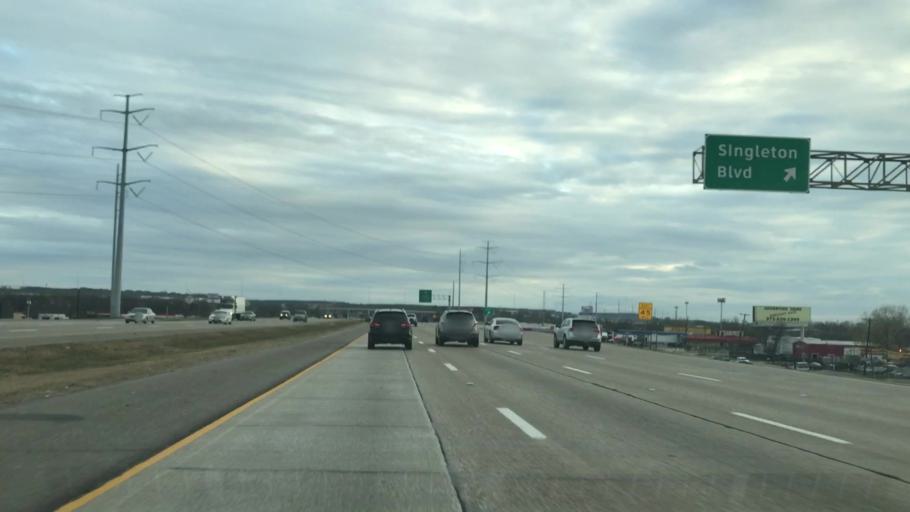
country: US
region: Texas
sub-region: Dallas County
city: Irving
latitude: 32.7811
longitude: -96.9177
